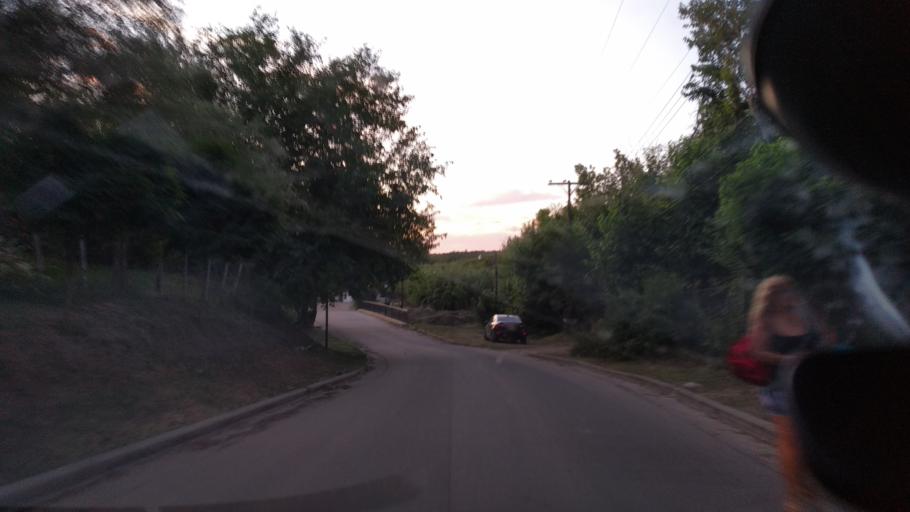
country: AR
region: Cordoba
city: Villa Las Rosas
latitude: -31.9440
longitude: -65.0663
